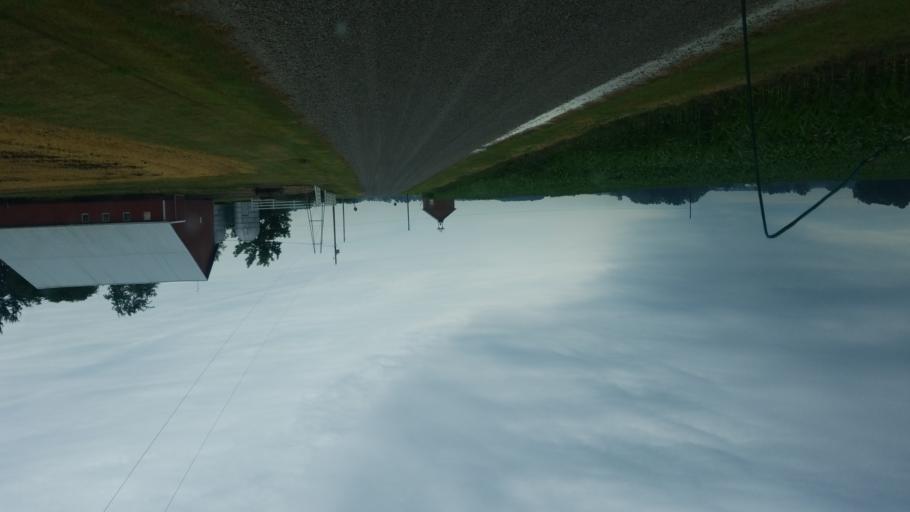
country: US
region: Indiana
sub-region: DeKalb County
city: Butler
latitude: 41.4514
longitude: -84.9099
